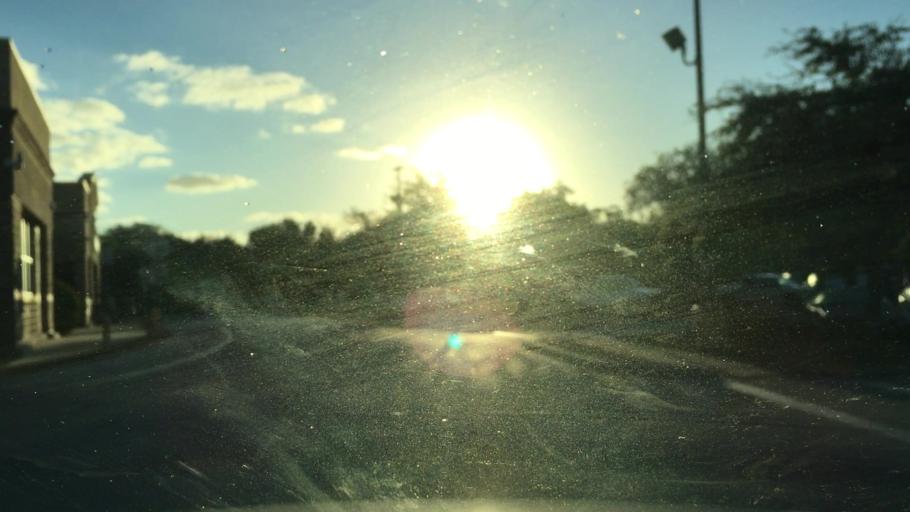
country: US
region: Florida
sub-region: Volusia County
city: Holly Hill
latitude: 29.2486
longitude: -81.0677
